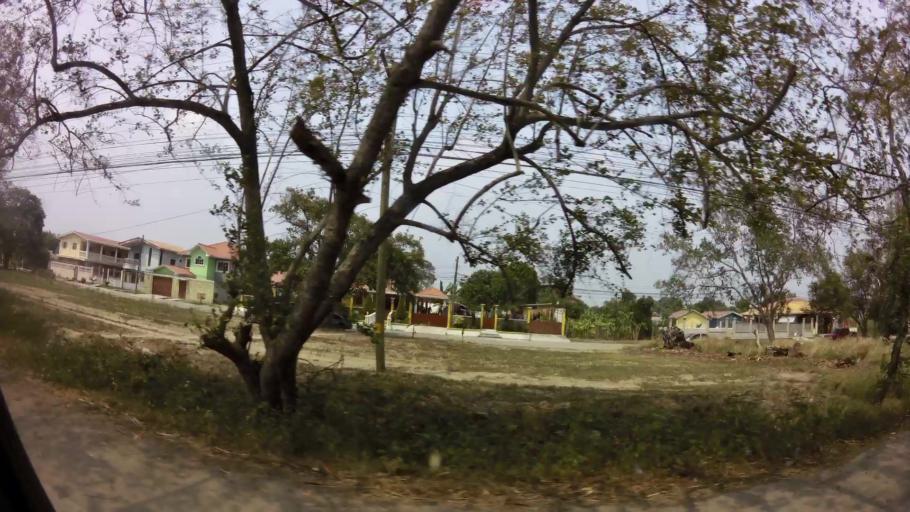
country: HN
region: Cortes
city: La Lima
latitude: 15.4305
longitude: -87.9015
